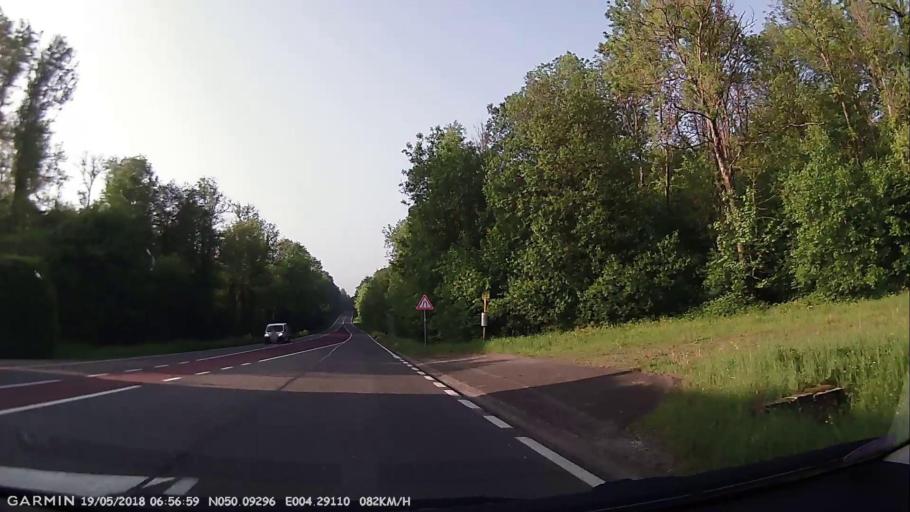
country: BE
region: Wallonia
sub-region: Province du Hainaut
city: Chimay
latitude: 50.0928
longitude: 4.2912
